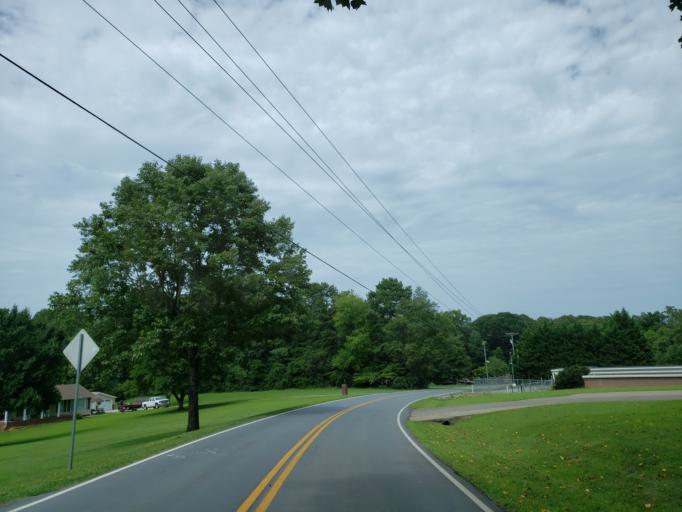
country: US
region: Georgia
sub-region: Pickens County
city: Jasper
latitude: 34.4461
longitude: -84.4198
